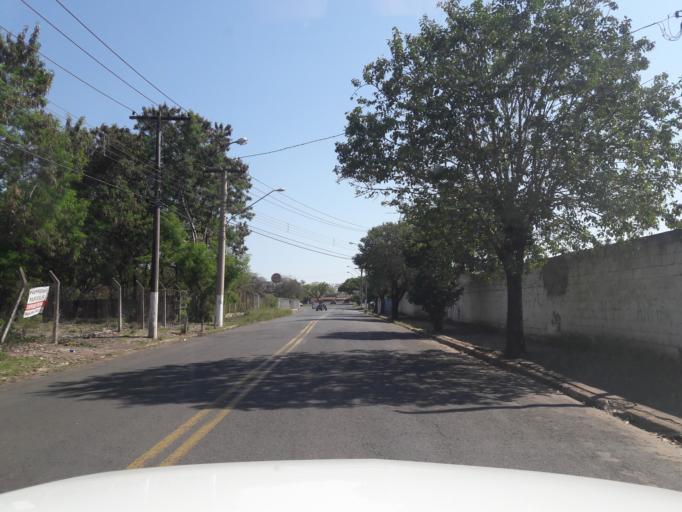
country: BR
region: Sao Paulo
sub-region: Moji-Guacu
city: Mogi-Gaucu
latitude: -22.3650
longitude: -46.9525
